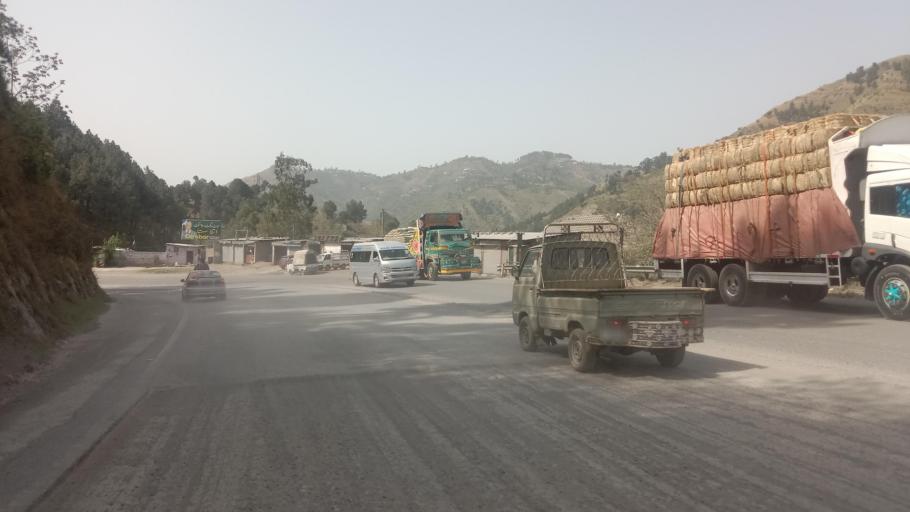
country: PK
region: Khyber Pakhtunkhwa
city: Abbottabad
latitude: 34.1222
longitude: 73.1846
